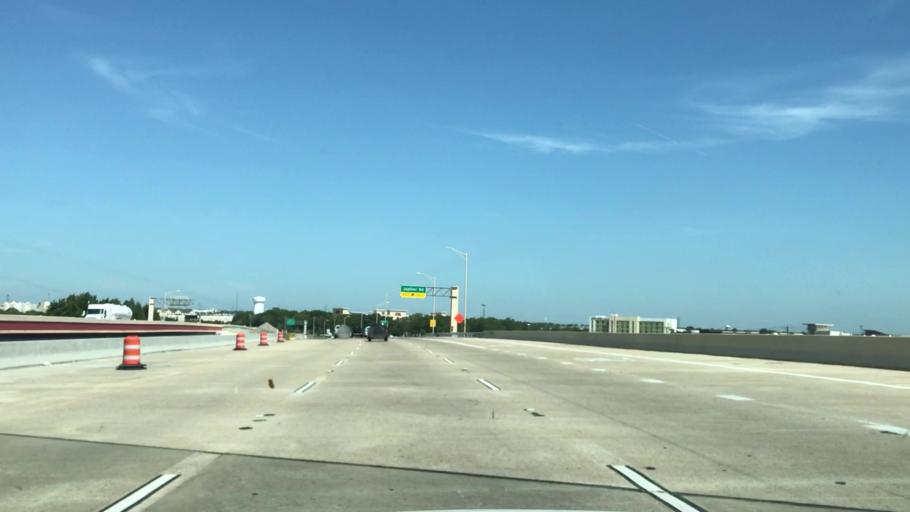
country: US
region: Texas
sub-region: Collin County
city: Plano
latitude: 32.9968
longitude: -96.6704
